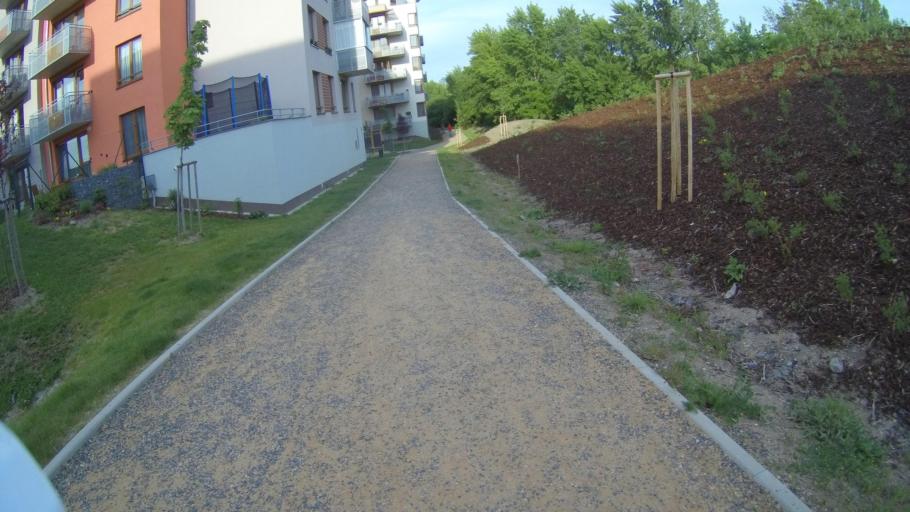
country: CZ
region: Praha
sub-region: Praha 18
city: Letnany
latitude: 50.1555
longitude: 14.5155
